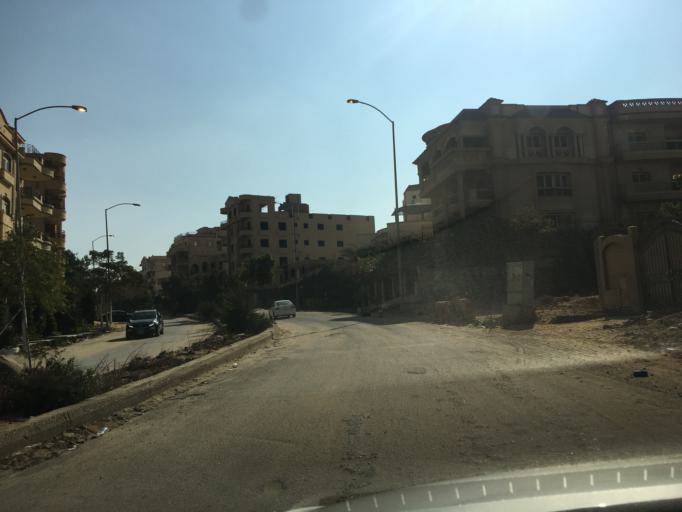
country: EG
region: Al Jizah
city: Awsim
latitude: 29.9997
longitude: 30.9871
